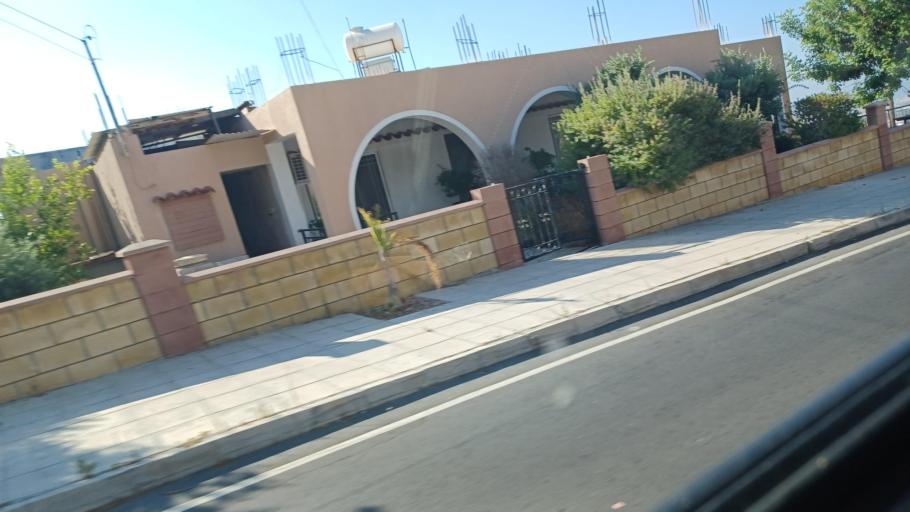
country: CY
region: Pafos
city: Tala
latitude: 34.8390
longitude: 32.4382
